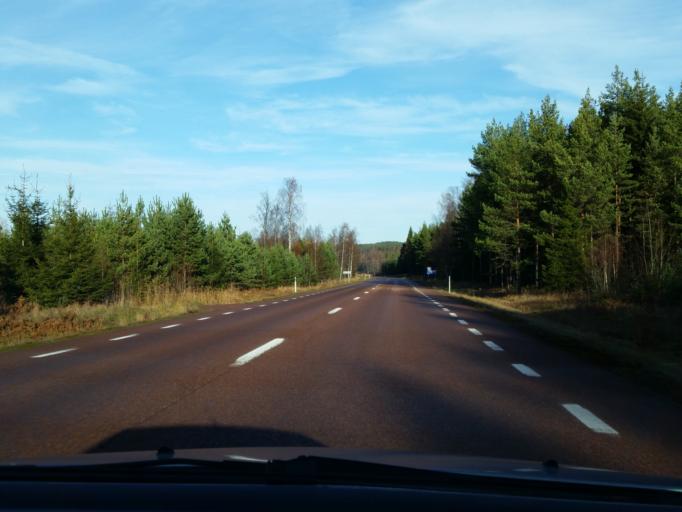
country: AX
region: Alands landsbygd
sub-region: Finstroem
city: Finstroem
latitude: 60.2910
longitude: 19.9533
